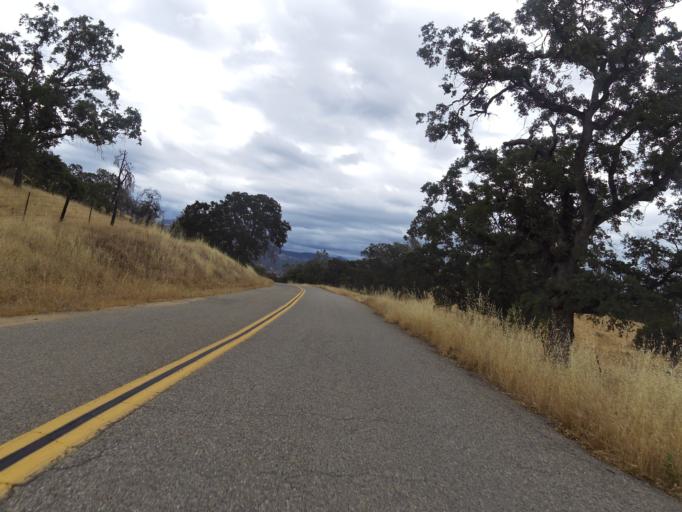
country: US
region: California
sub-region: Madera County
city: Yosemite Lakes
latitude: 37.2844
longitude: -119.8117
